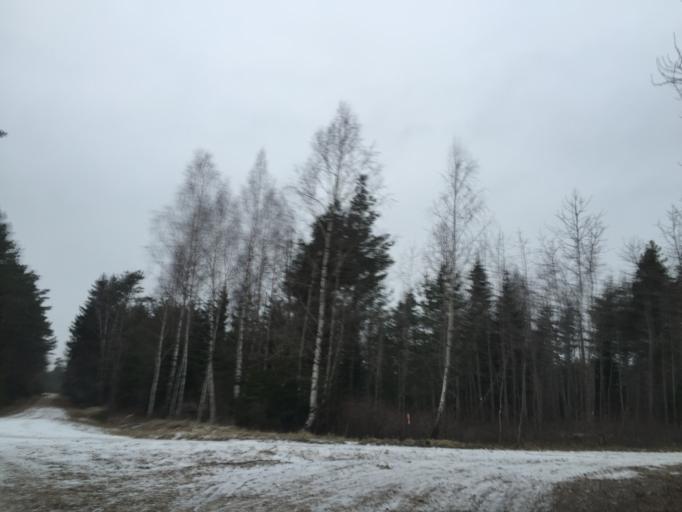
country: EE
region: Saare
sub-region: Kuressaare linn
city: Kuressaare
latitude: 58.3993
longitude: 22.1985
